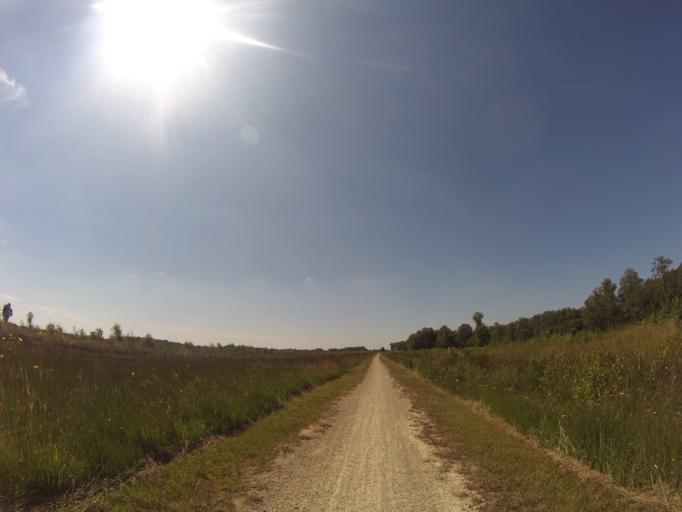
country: DE
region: Lower Saxony
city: Twist
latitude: 52.6619
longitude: 7.0137
